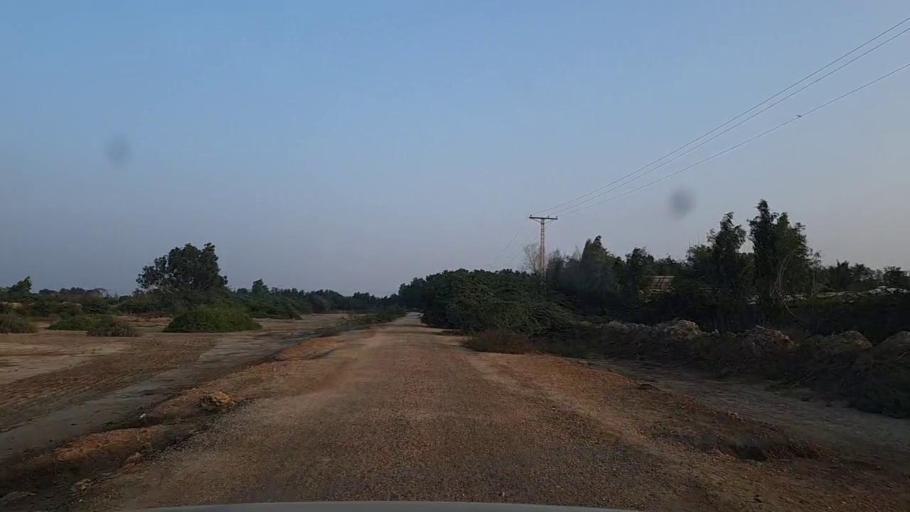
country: PK
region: Sindh
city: Mirpur Sakro
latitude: 24.6125
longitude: 67.5953
